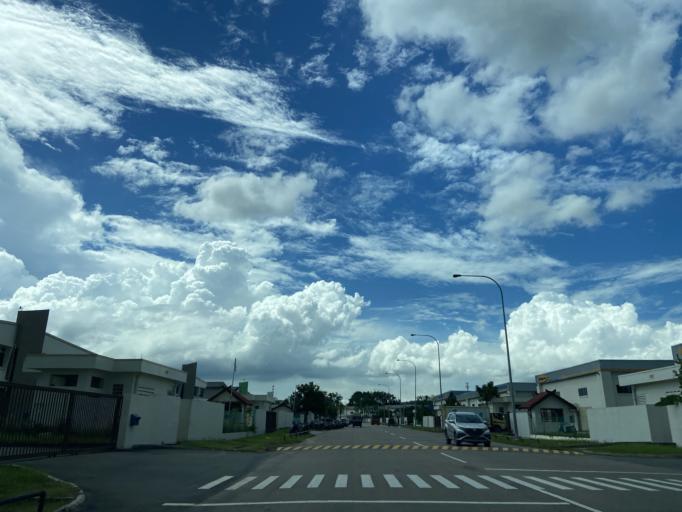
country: SG
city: Singapore
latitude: 1.0593
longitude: 104.0333
